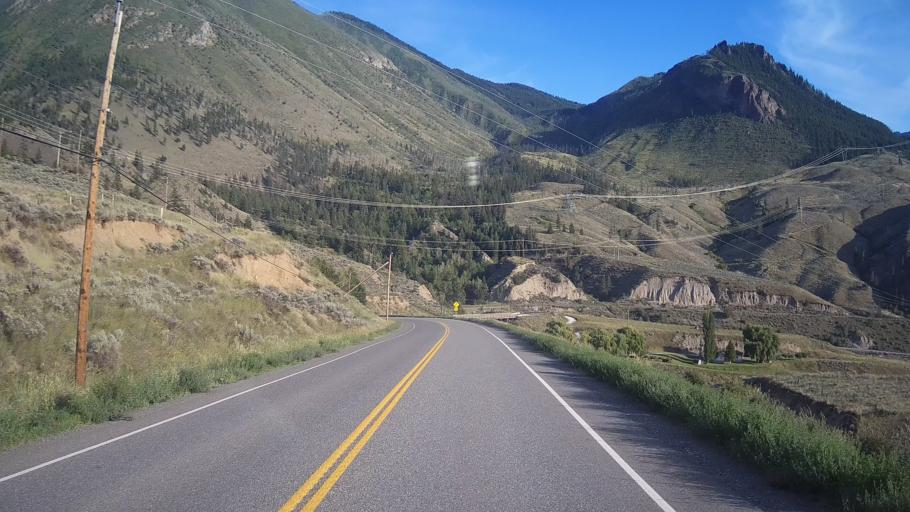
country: CA
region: British Columbia
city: Lillooet
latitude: 50.7610
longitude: -121.8346
